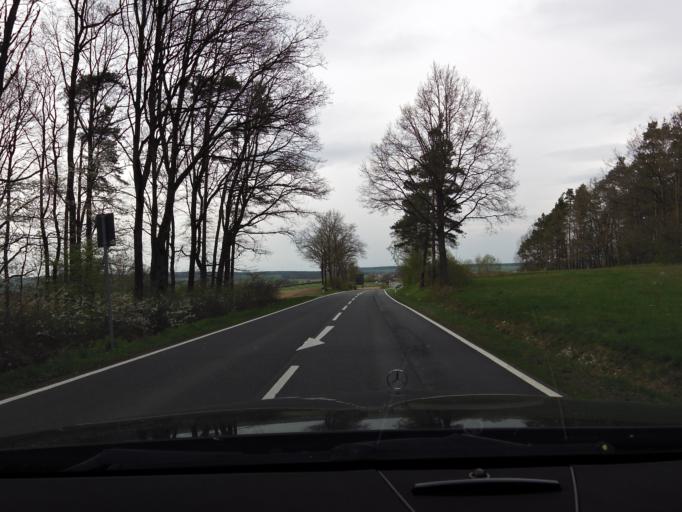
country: DE
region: Bavaria
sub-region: Upper Franconia
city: Pommersfelden
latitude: 49.7449
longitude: 10.8163
